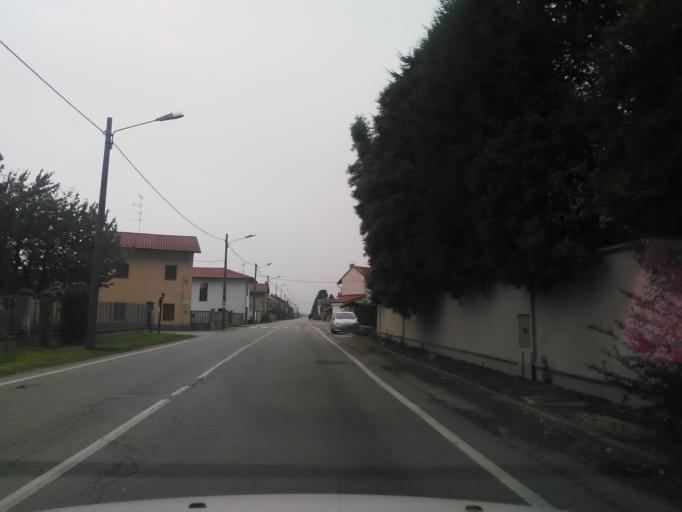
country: IT
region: Piedmont
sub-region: Provincia di Vercelli
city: Bianze
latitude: 45.3051
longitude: 8.1193
